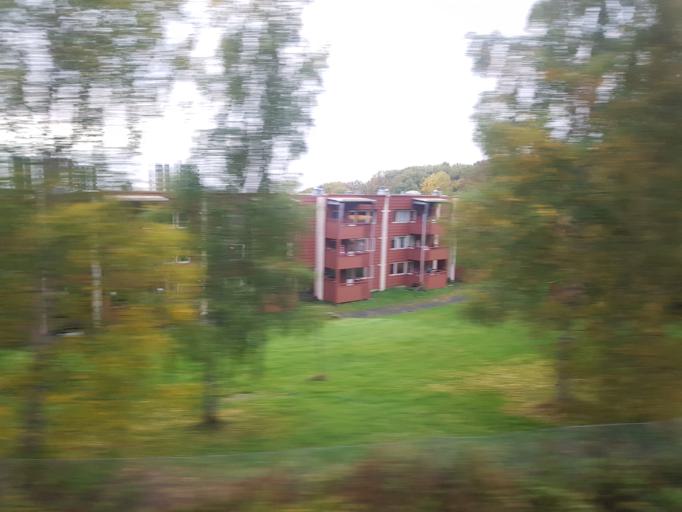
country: NO
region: Sor-Trondelag
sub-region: Trondheim
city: Trondheim
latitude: 63.3781
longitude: 10.3629
